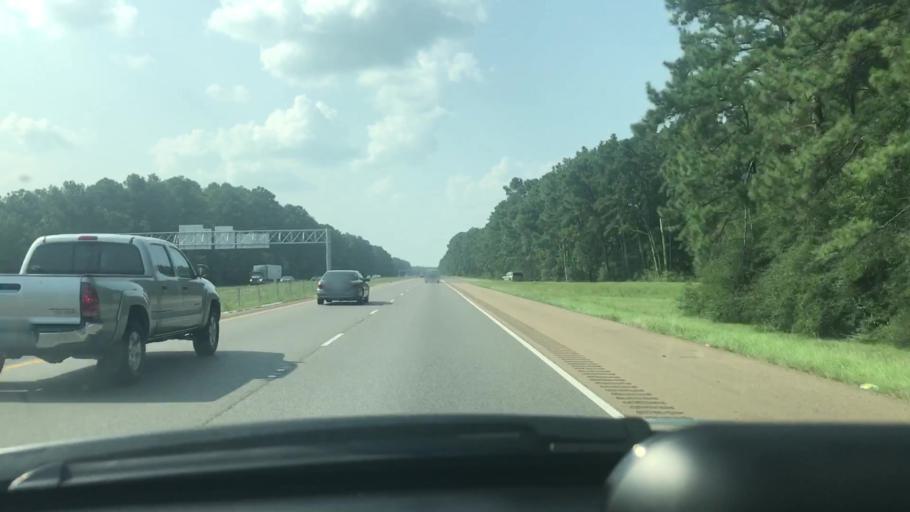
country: US
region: Louisiana
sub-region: Tangipahoa Parish
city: Hammond
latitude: 30.4808
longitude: -90.4918
